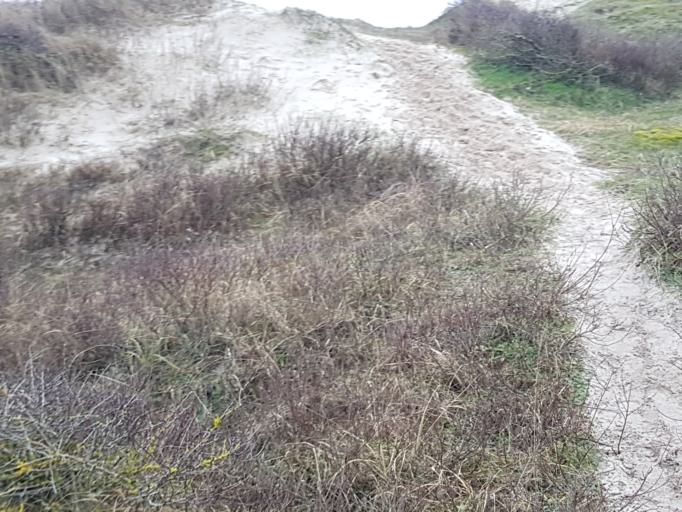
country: NL
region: North Holland
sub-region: Gemeente Bergen
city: Egmond aan Zee
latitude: 52.6375
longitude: 4.6280
